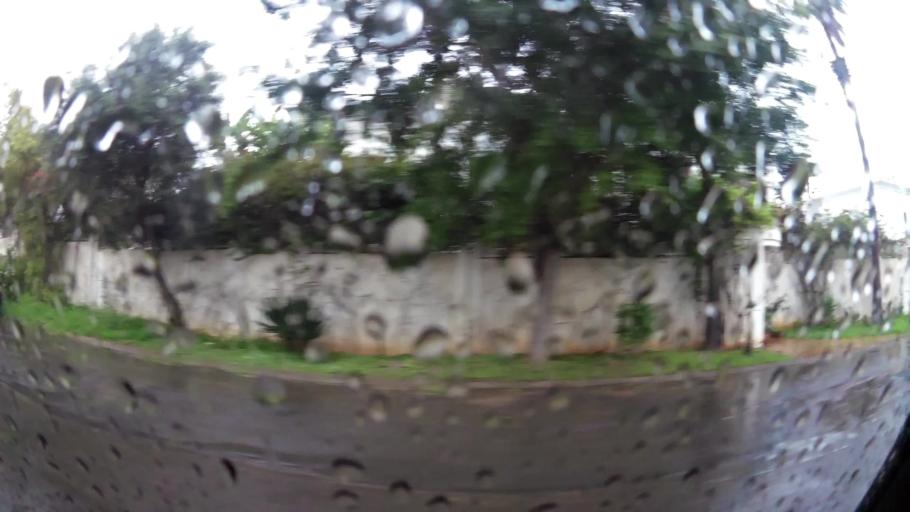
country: MA
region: Grand Casablanca
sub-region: Casablanca
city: Casablanca
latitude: 33.5869
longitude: -7.6738
